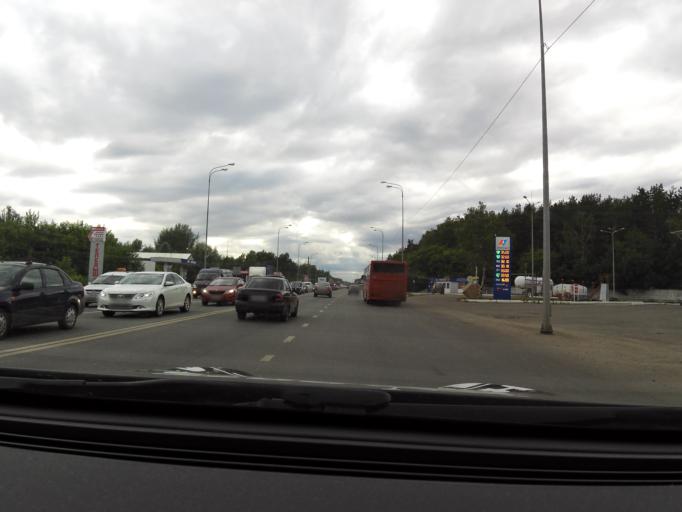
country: RU
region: Tatarstan
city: Staroye Arakchino
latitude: 55.8272
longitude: 49.0228
